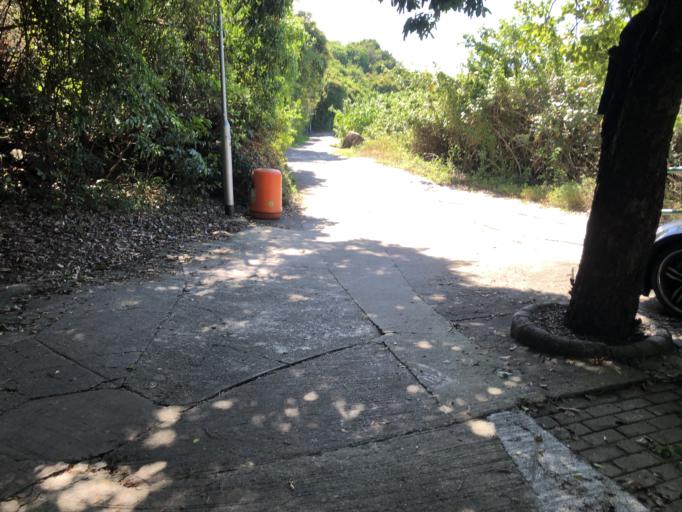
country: HK
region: Tuen Mun
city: Tuen Mun
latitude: 22.2973
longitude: 113.9691
